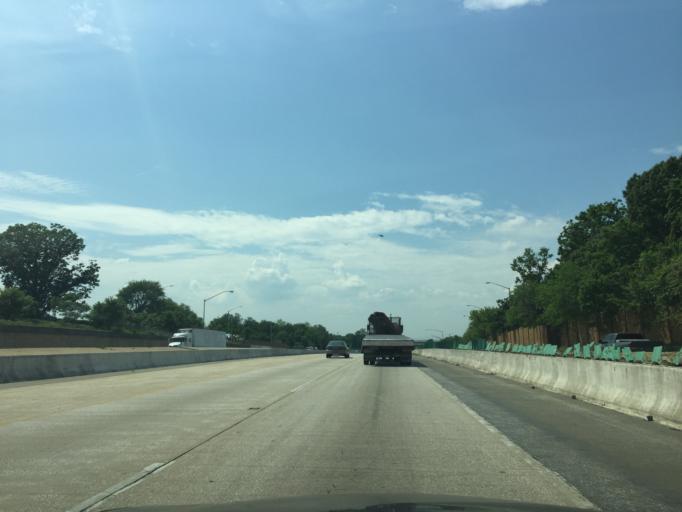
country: US
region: Maryland
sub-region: Anne Arundel County
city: Pumphrey
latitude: 39.2032
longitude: -76.6356
